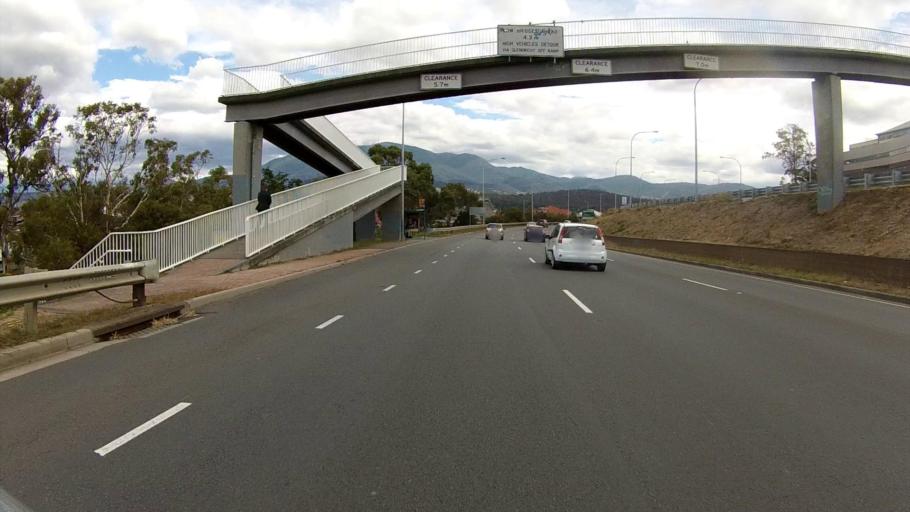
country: AU
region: Tasmania
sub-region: Clarence
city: Lindisfarne
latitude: -42.8629
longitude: 147.3598
